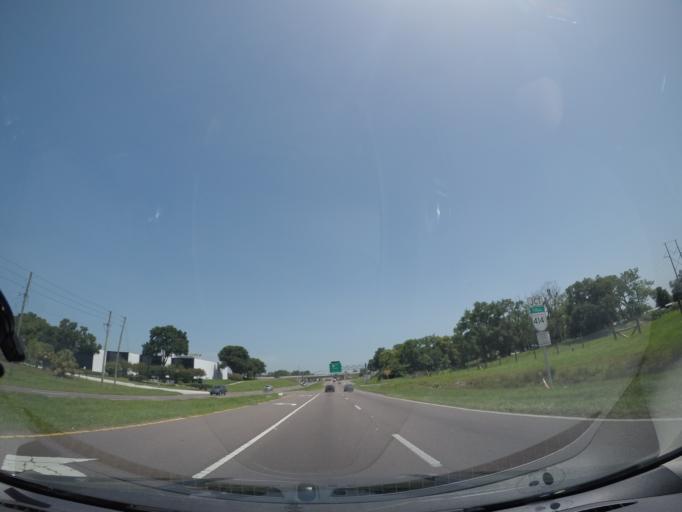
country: US
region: Florida
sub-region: Orange County
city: Lockhart
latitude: 28.6376
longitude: -81.4549
